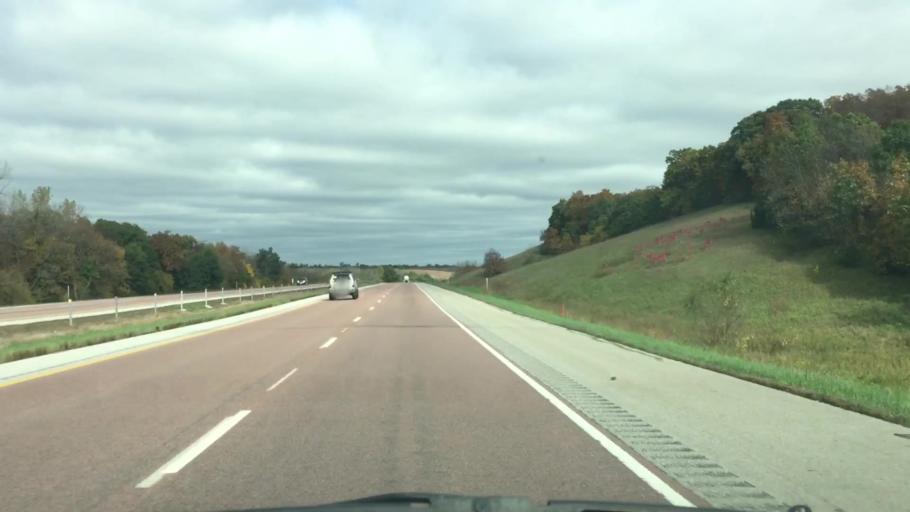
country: US
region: Iowa
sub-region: Clarke County
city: Osceola
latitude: 41.1912
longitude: -93.7856
